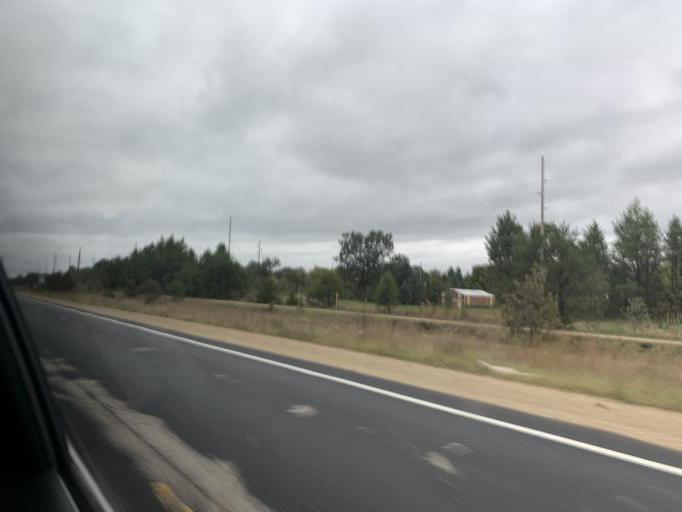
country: US
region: Wisconsin
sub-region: Richland County
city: Richland Center
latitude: 43.2080
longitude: -90.2624
